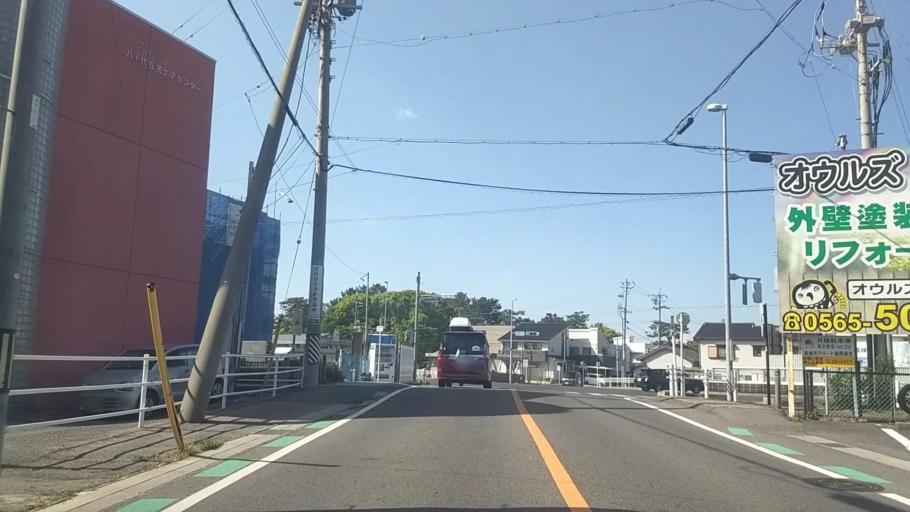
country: JP
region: Aichi
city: Anjo
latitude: 34.9889
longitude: 137.0837
